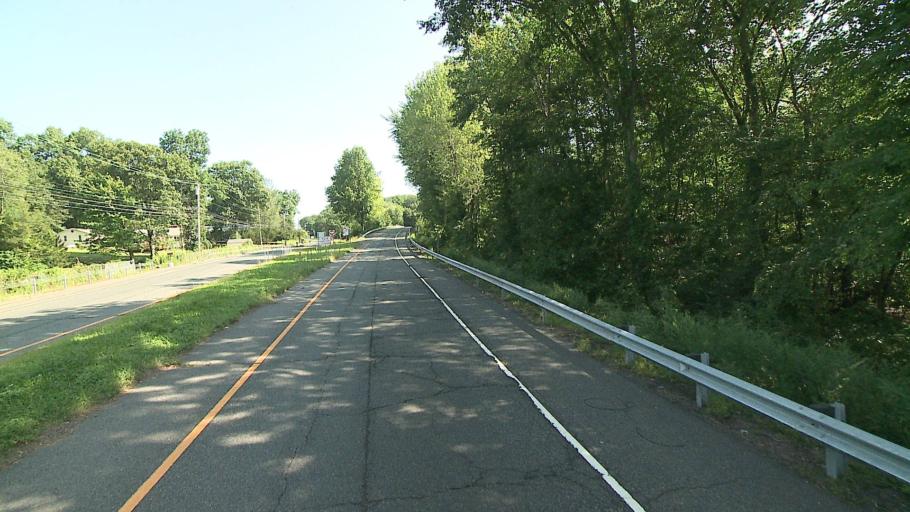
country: US
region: Connecticut
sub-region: New Haven County
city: Meriden
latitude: 41.5571
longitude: -72.7775
